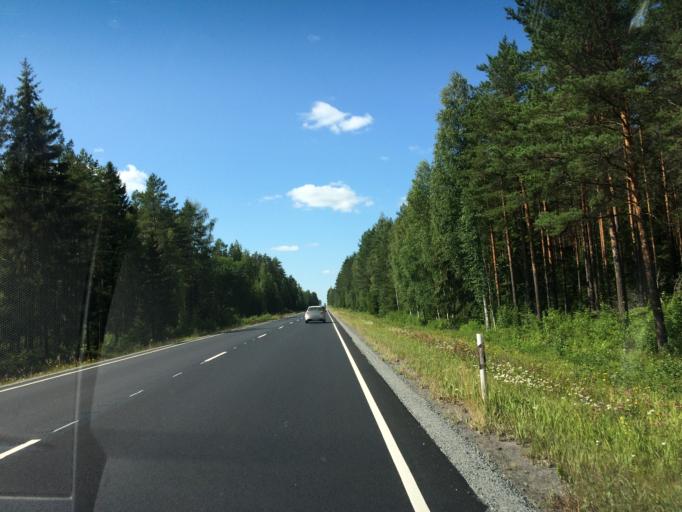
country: FI
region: Pirkanmaa
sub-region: Lounais-Pirkanmaa
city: Kiikoinen
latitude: 61.4735
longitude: 22.5022
